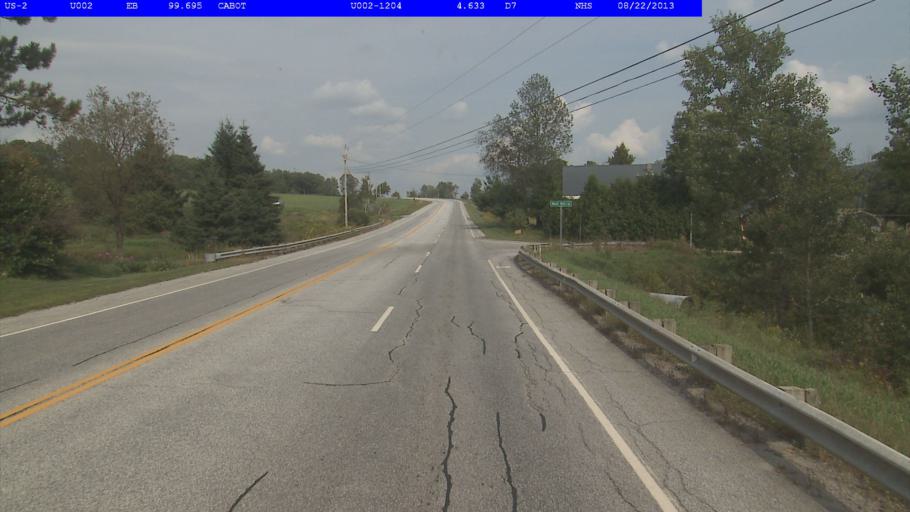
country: US
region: Vermont
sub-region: Caledonia County
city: Hardwick
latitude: 44.3898
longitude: -72.2514
